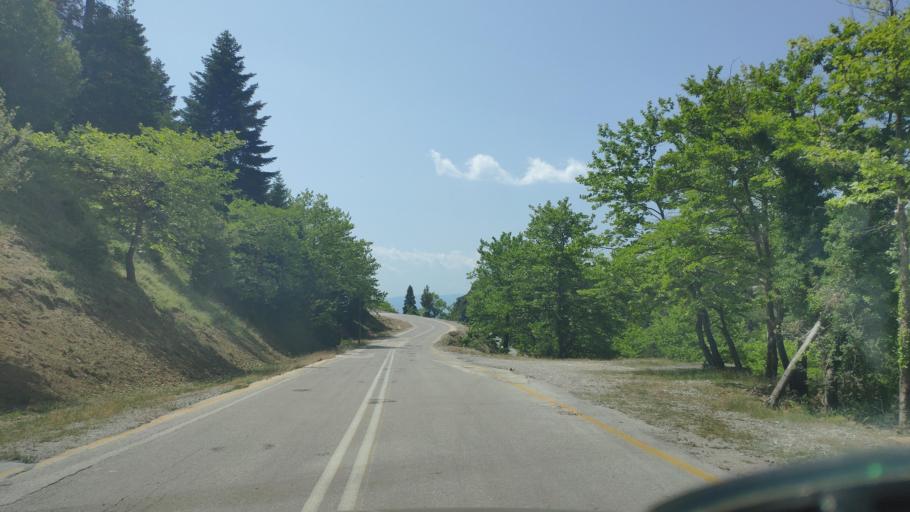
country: GR
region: Epirus
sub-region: Nomos Artas
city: Ano Kalentini
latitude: 39.2502
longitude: 21.2455
